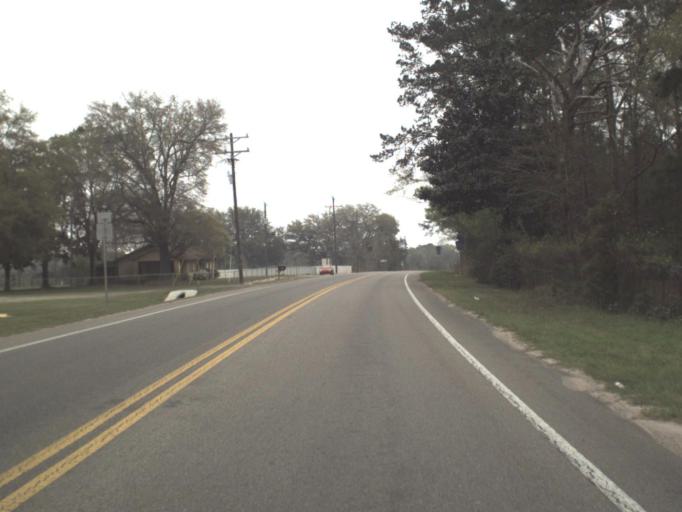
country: US
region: Florida
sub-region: Gadsden County
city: Gretna
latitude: 30.5930
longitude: -84.6669
